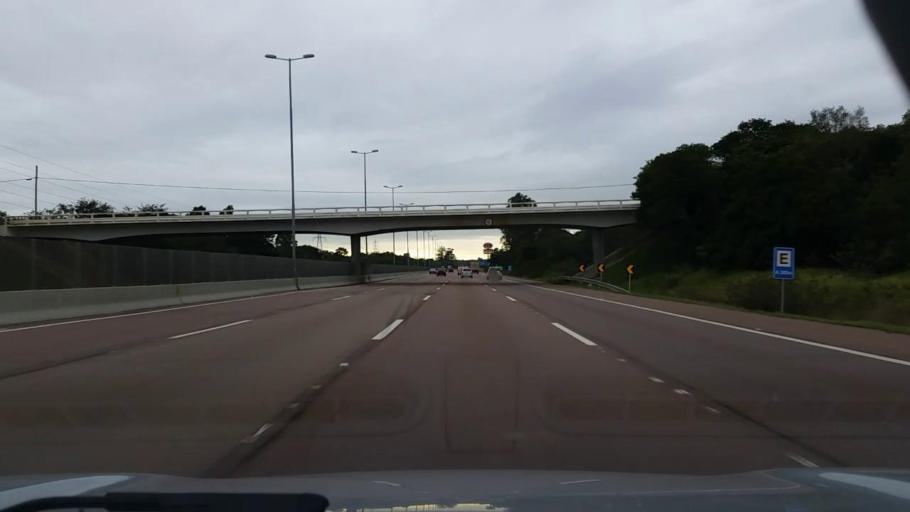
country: BR
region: Rio Grande do Sul
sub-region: Cachoeirinha
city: Cachoeirinha
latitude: -29.9538
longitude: -51.0596
